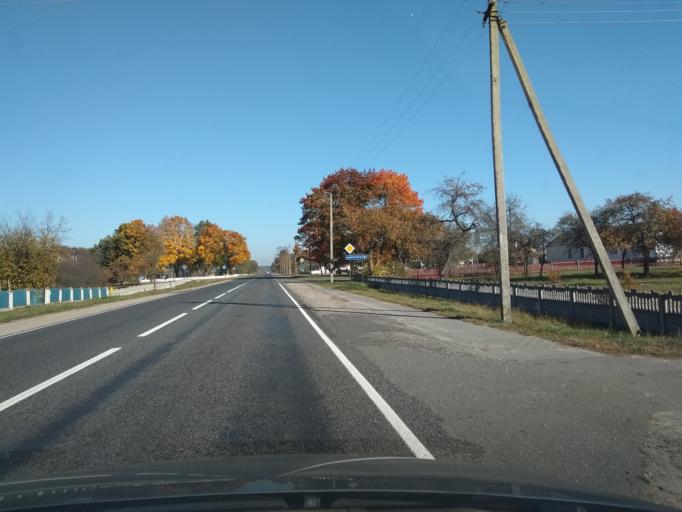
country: BY
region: Brest
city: Malaryta
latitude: 51.9859
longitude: 24.2058
